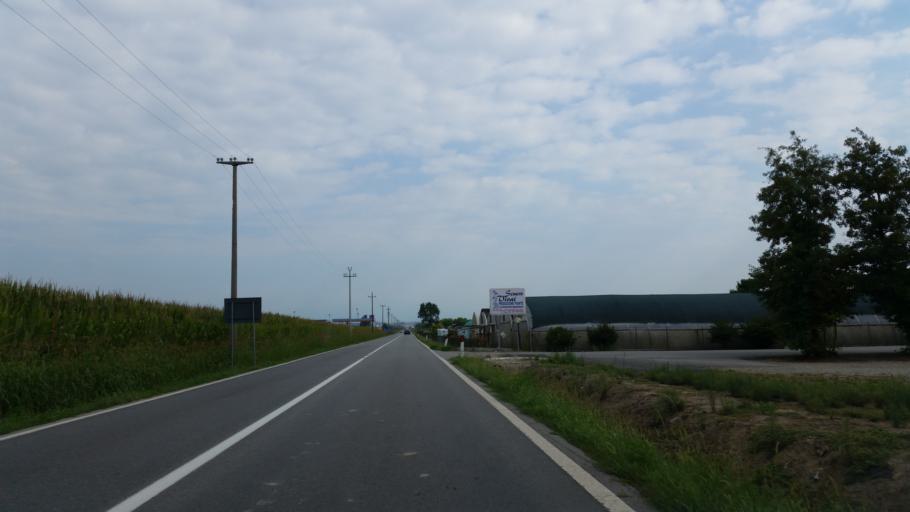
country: IT
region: Piedmont
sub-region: Provincia di Torino
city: Montanaro
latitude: 45.2390
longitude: 7.8912
